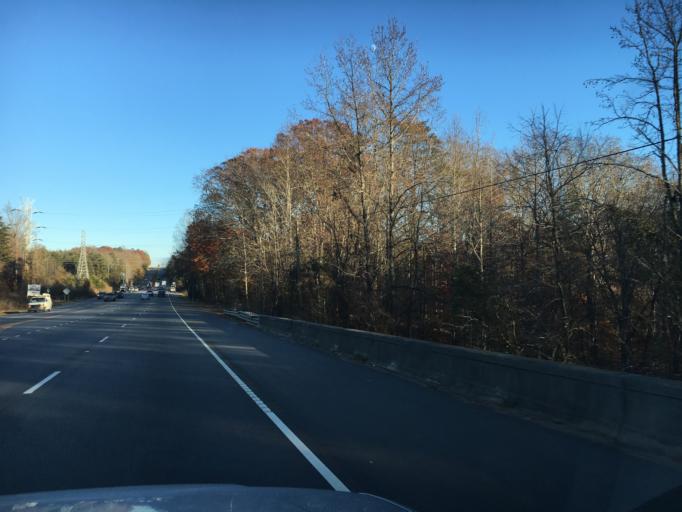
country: US
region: South Carolina
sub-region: Spartanburg County
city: Duncan
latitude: 34.9555
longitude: -82.1582
